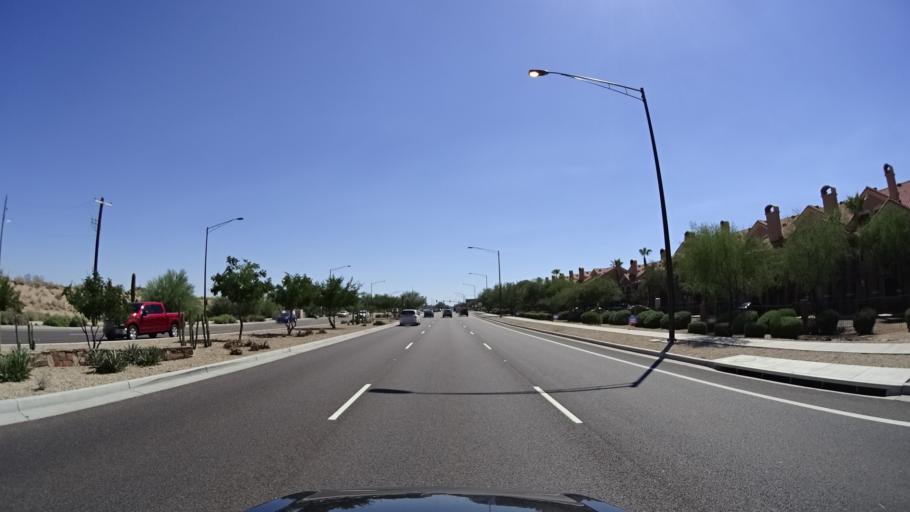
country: US
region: Arizona
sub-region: Maricopa County
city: Paradise Valley
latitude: 33.6438
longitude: -111.9254
